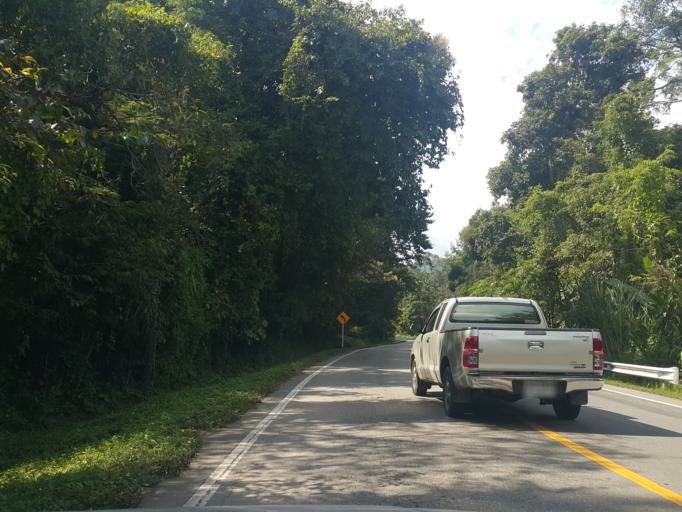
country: TH
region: Chiang Mai
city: Chom Thong
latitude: 18.5400
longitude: 98.5973
